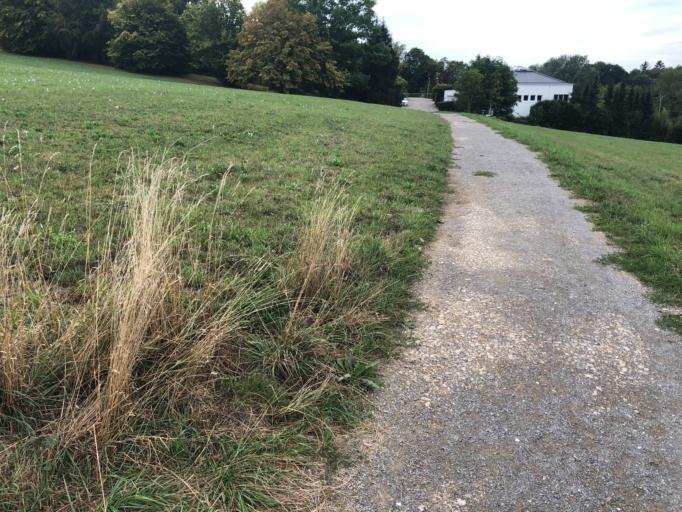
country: DE
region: Baden-Wuerttemberg
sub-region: Tuebingen Region
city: Tuebingen
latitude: 48.5247
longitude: 9.0676
